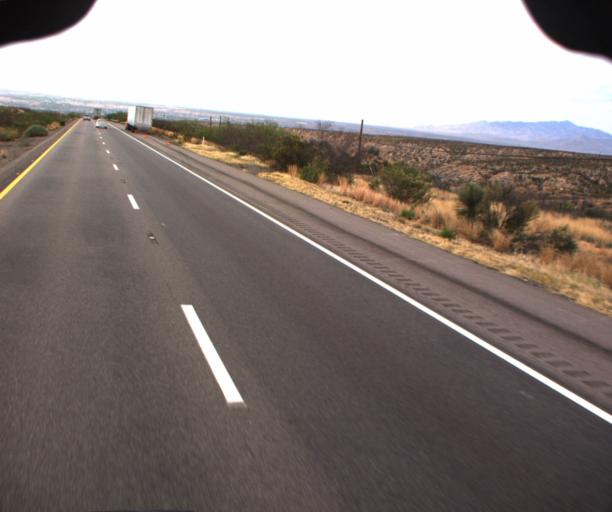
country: US
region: Arizona
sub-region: Cochise County
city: Saint David
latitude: 31.9842
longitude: -110.2021
